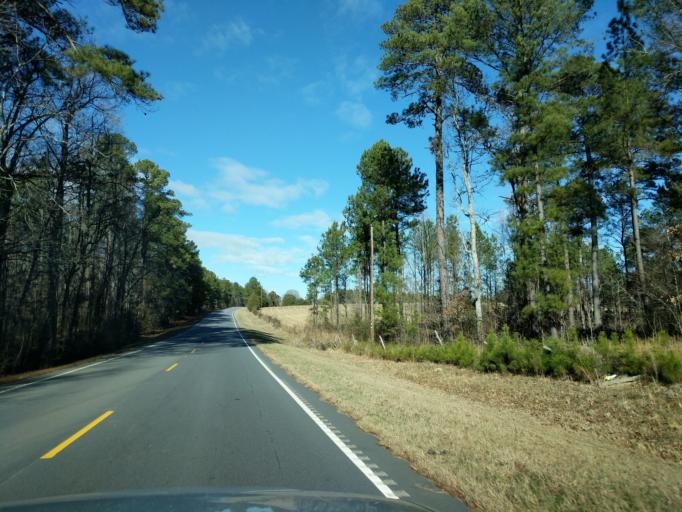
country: US
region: South Carolina
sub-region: Edgefield County
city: Edgefield
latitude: 33.9399
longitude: -82.0481
